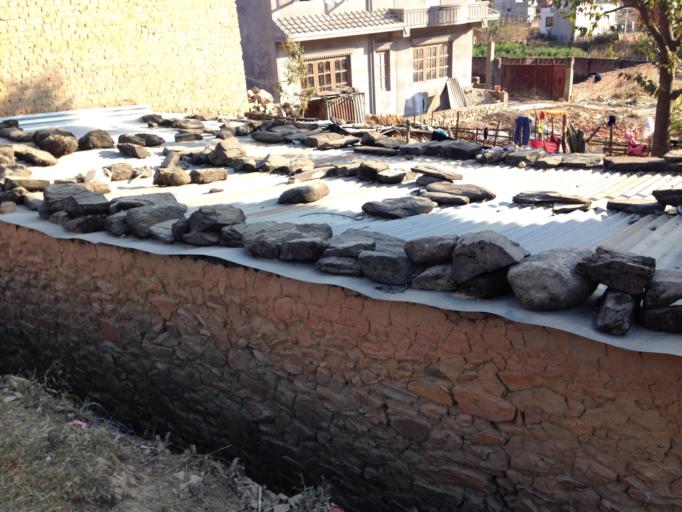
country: NP
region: Central Region
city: Kirtipur
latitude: 27.7242
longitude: 85.2732
